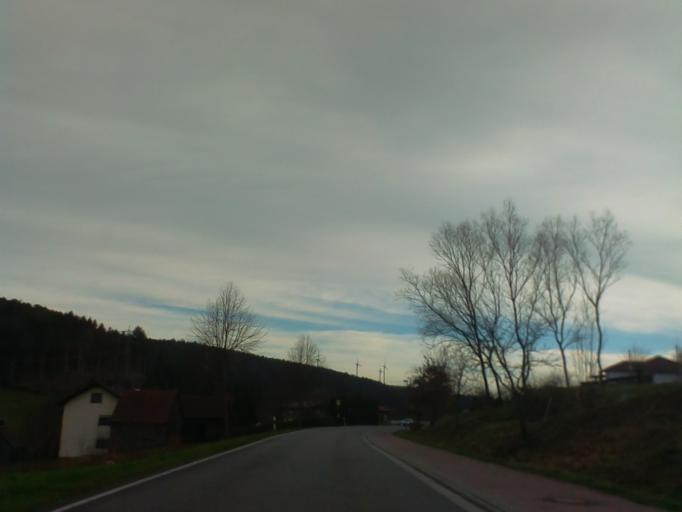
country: DE
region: Hesse
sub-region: Regierungsbezirk Darmstadt
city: Erbach
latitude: 49.6639
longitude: 8.9254
